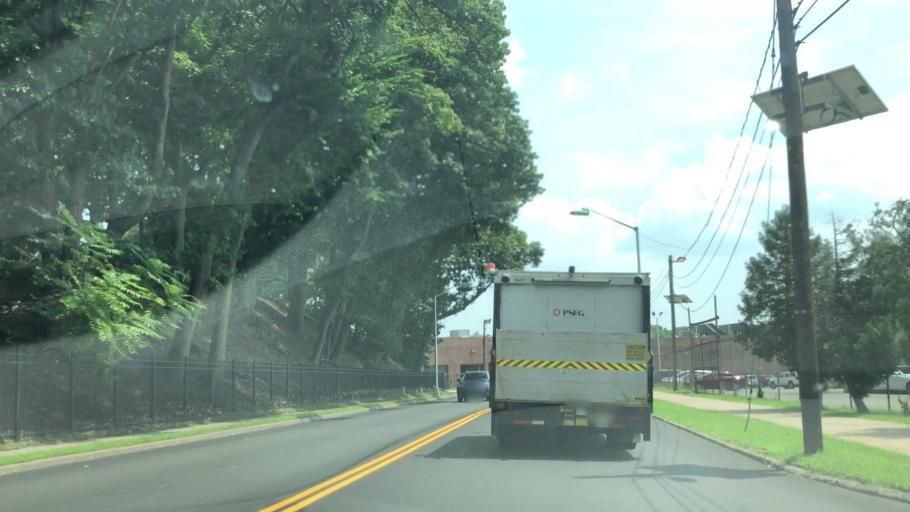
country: US
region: New Jersey
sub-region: Essex County
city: Orange
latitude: 40.7825
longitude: -74.2239
